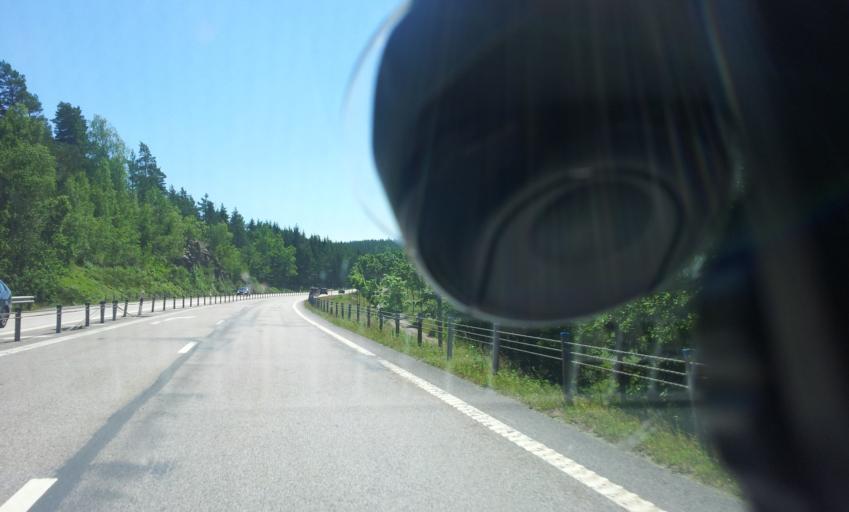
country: SE
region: Kalmar
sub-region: Vasterviks Kommun
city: Forserum
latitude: 58.0255
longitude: 16.5177
